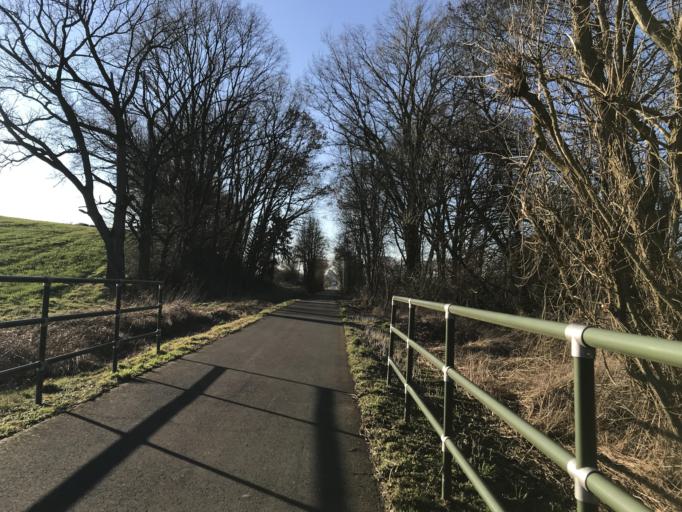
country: DE
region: Hesse
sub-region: Regierungsbezirk Kassel
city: Schrecksbach
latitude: 50.8743
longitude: 9.2795
